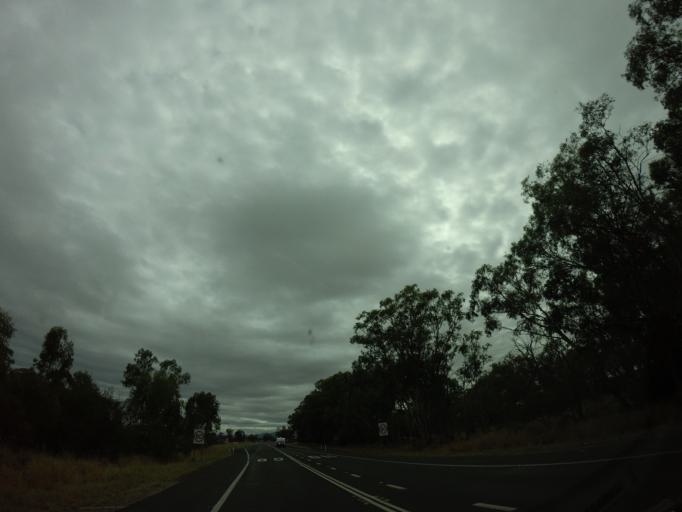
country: AU
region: New South Wales
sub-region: Narrabri
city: Narrabri
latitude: -30.3504
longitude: 149.7550
